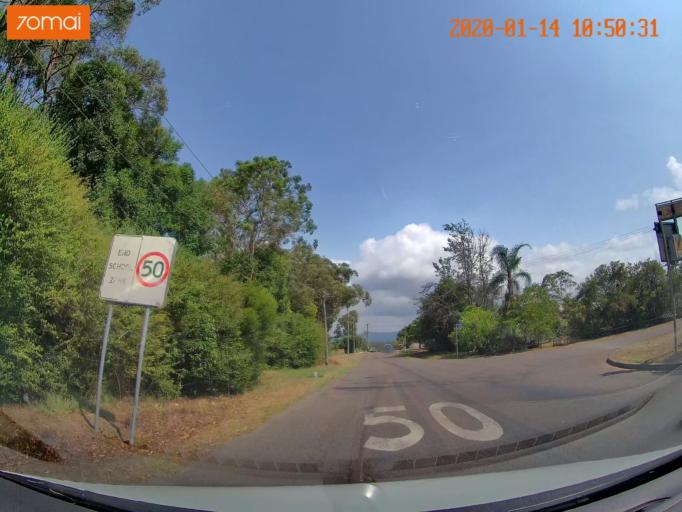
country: AU
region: New South Wales
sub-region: Lake Macquarie Shire
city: Dora Creek
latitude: -33.1027
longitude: 151.4867
